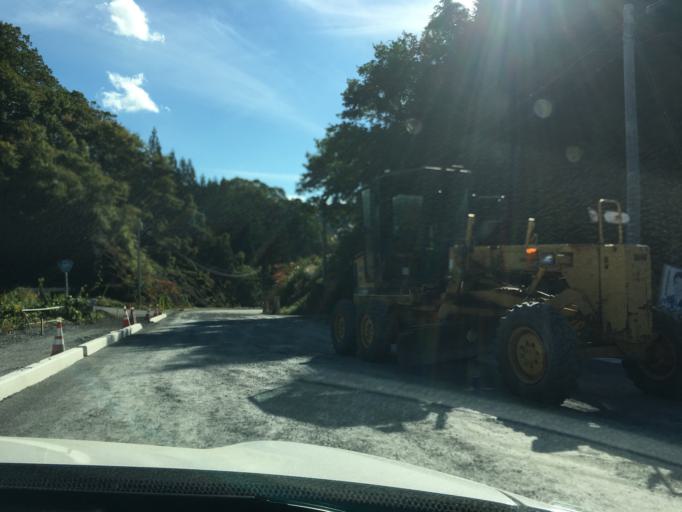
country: JP
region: Fukushima
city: Ishikawa
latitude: 37.1313
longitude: 140.5918
